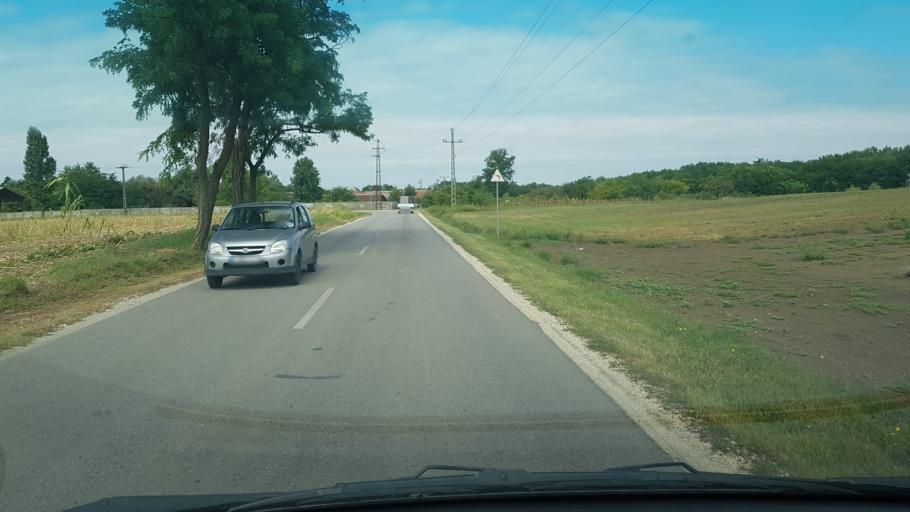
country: HU
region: Pest
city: Dunavarsany
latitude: 47.2870
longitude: 19.0416
